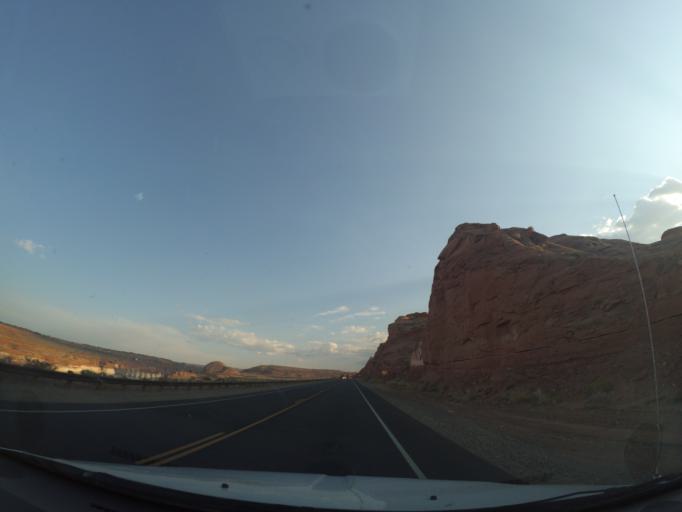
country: US
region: Arizona
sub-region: Coconino County
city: Page
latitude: 36.9518
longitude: -111.4932
